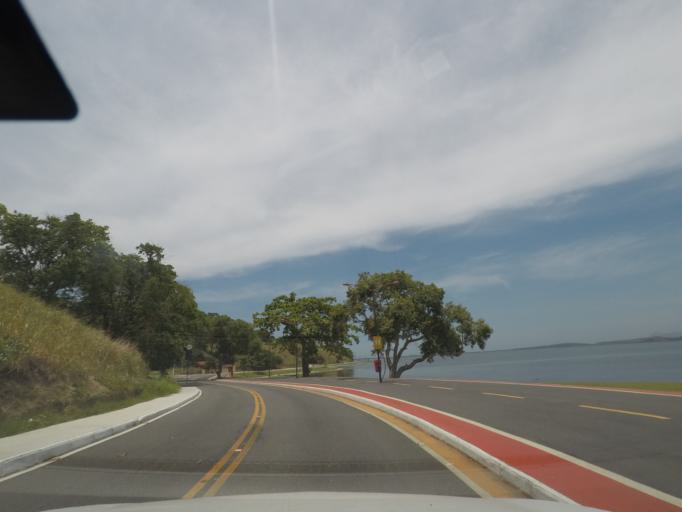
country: BR
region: Rio de Janeiro
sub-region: Marica
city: Marica
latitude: -22.9314
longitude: -42.8277
